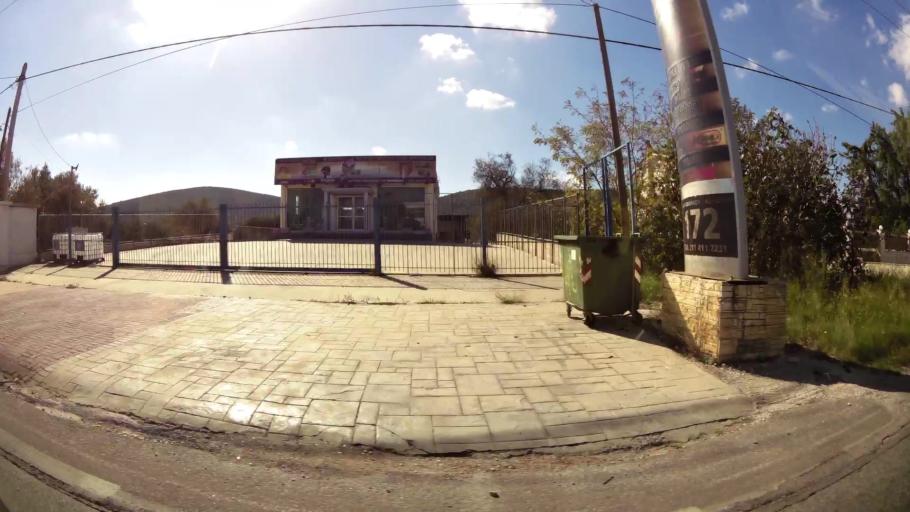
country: GR
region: Attica
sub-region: Nomarchia Anatolikis Attikis
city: Markopoulo
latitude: 37.8867
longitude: 23.9097
